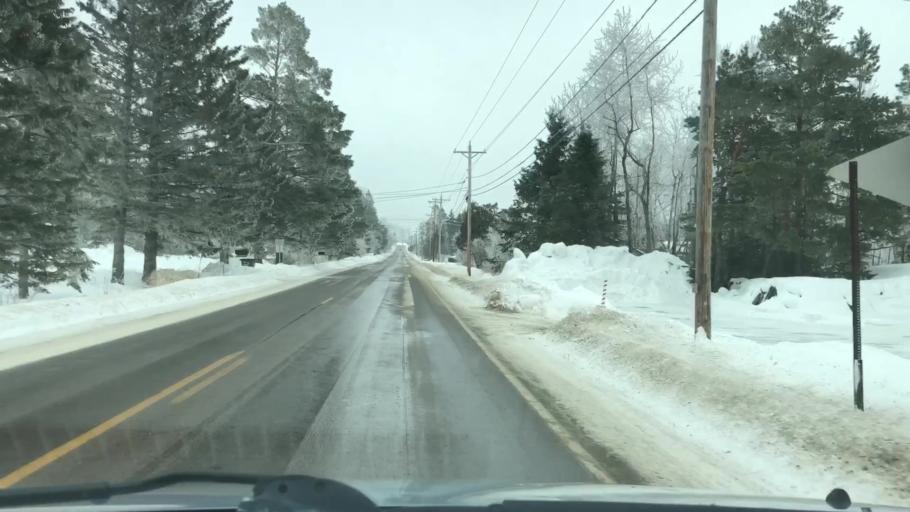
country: US
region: Minnesota
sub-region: Saint Louis County
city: Arnold
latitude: 46.8595
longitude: -92.1203
